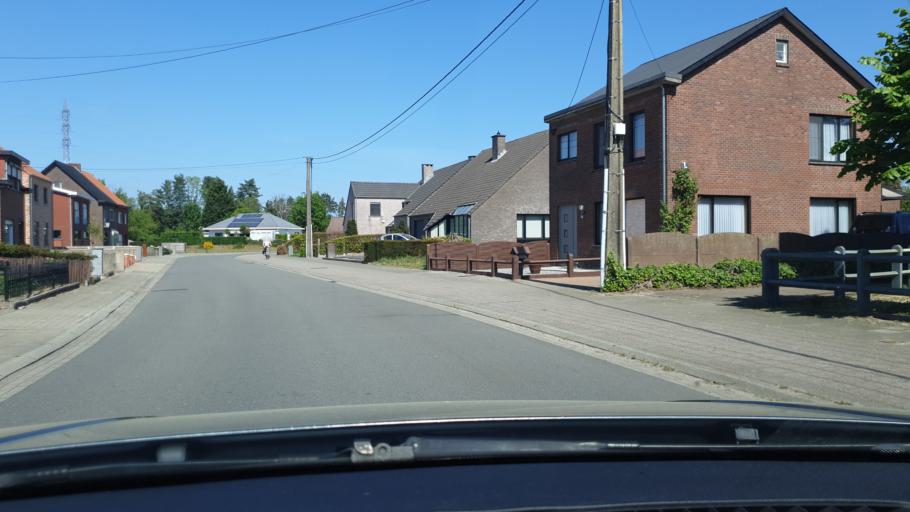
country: BE
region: Flanders
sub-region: Provincie Antwerpen
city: Geel
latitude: 51.1736
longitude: 4.9784
